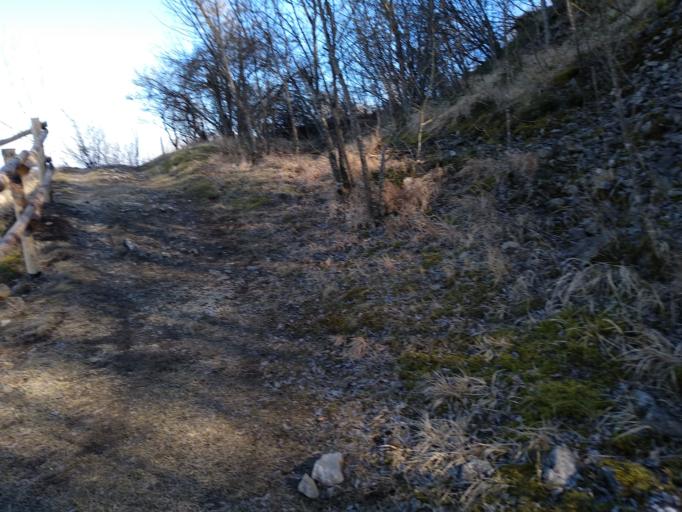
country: IT
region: Emilia-Romagna
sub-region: Provincia di Reggio Emilia
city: Castelnovo ne'Monti
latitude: 44.4265
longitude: 10.4193
